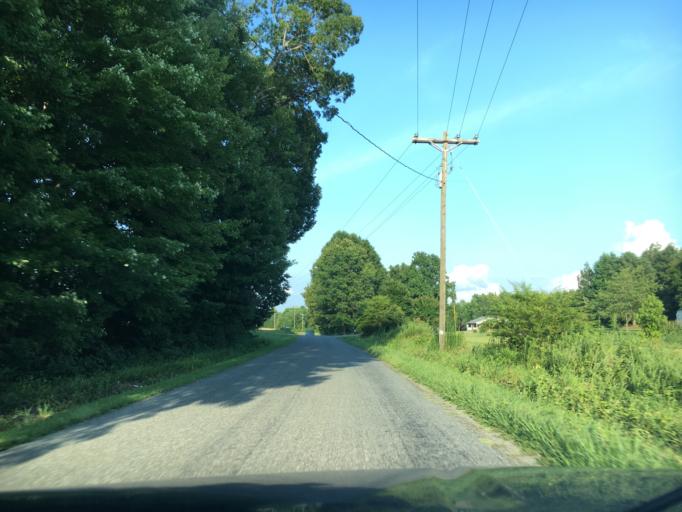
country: US
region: Virginia
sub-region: Pittsylvania County
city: Gretna
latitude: 36.8428
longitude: -79.2034
